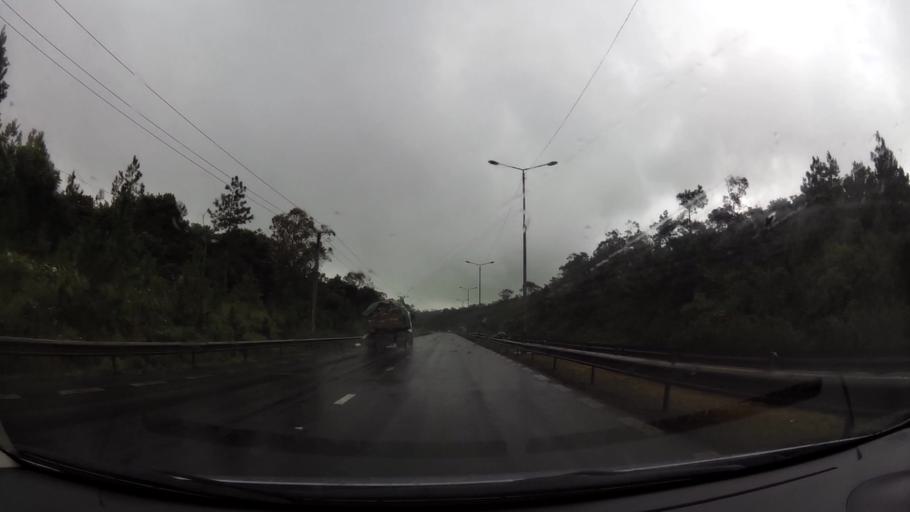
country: MU
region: Plaines Wilhems
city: Midlands
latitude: -20.3278
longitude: 57.5473
